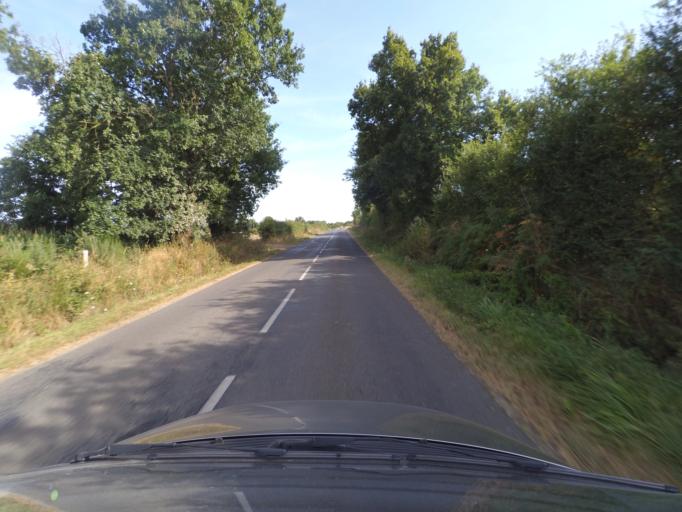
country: FR
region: Pays de la Loire
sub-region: Departement de la Loire-Atlantique
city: Montbert
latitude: 47.0462
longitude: -1.4810
